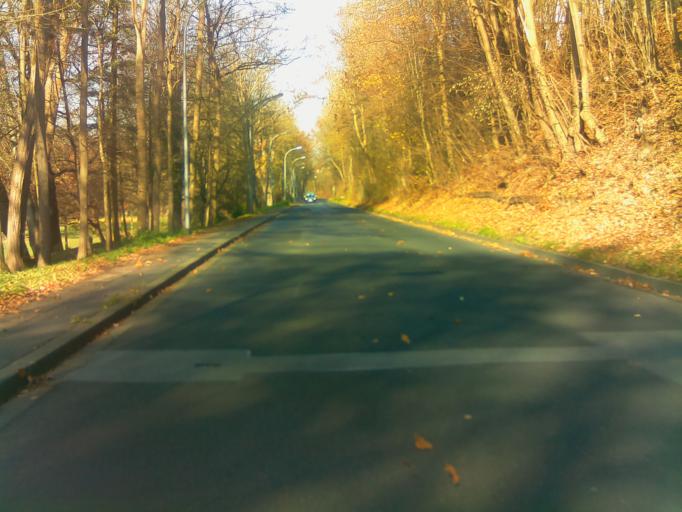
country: DE
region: Bavaria
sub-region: Regierungsbezirk Unterfranken
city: Bad Kissingen
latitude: 50.2103
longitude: 10.0727
